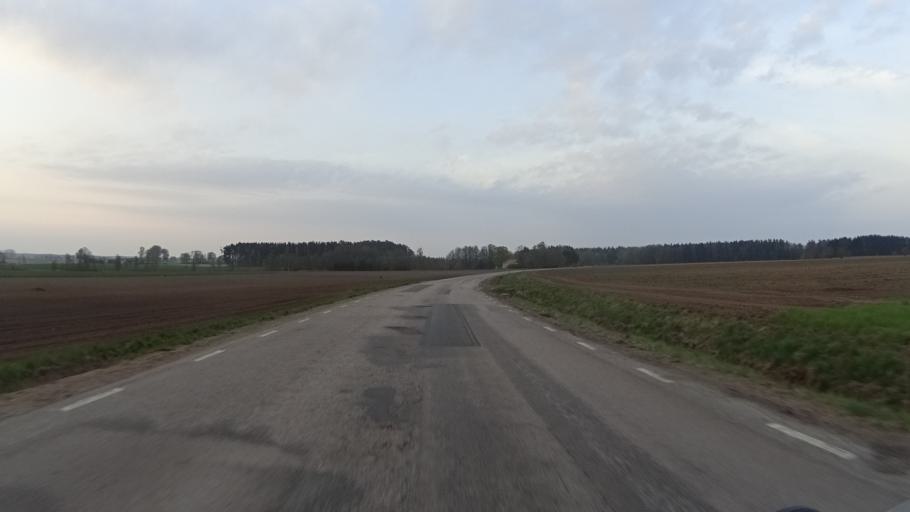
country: SE
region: Vaestra Goetaland
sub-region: Gotene Kommun
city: Kallby
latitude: 58.4927
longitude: 13.3153
